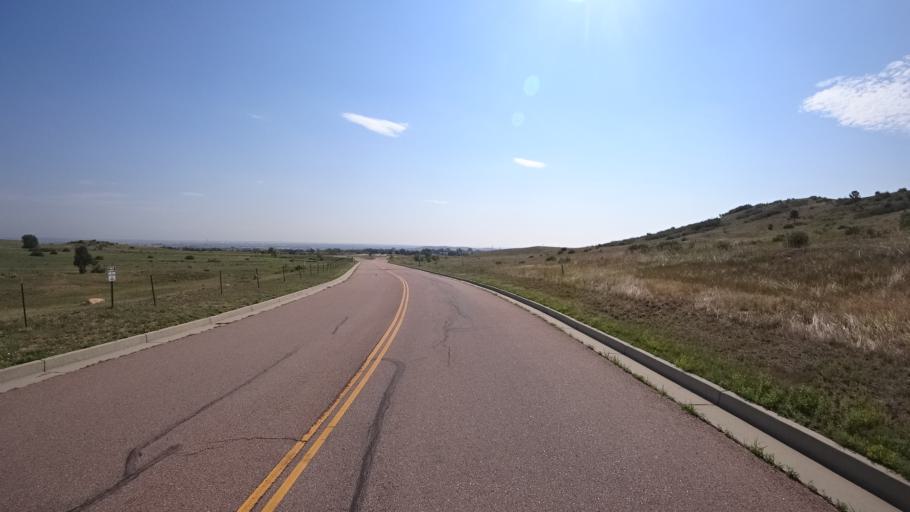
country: US
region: Colorado
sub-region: El Paso County
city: Fort Carson
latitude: 38.7370
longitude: -104.8136
